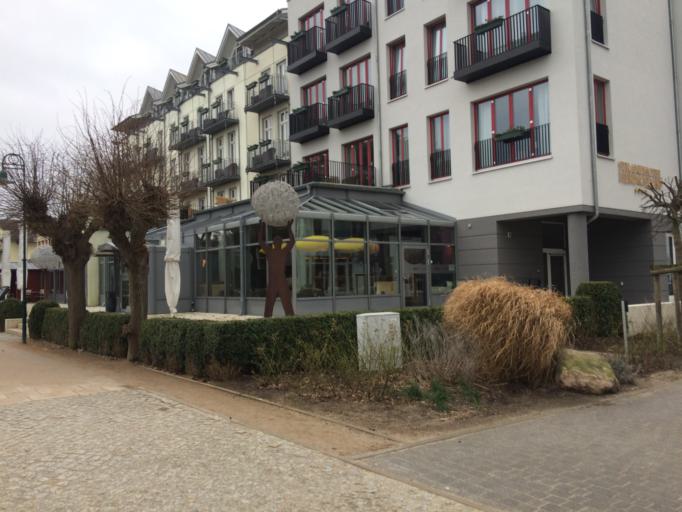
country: DE
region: Mecklenburg-Vorpommern
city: Seebad Heringsdorf
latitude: 53.9510
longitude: 14.1750
